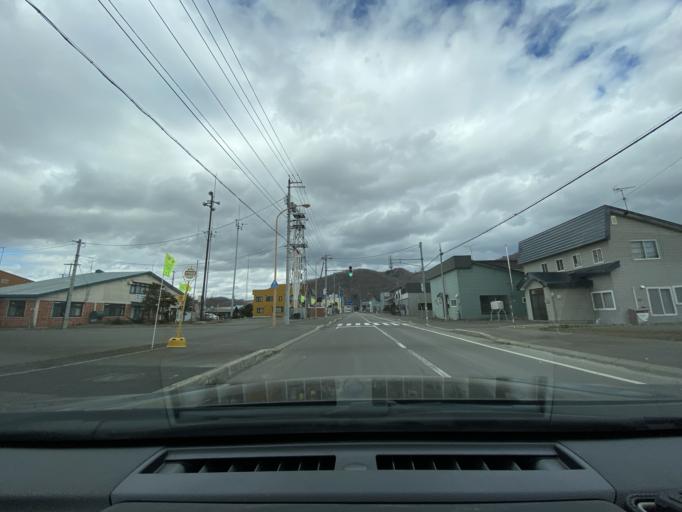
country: JP
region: Hokkaido
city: Nayoro
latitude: 44.1338
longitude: 142.4863
